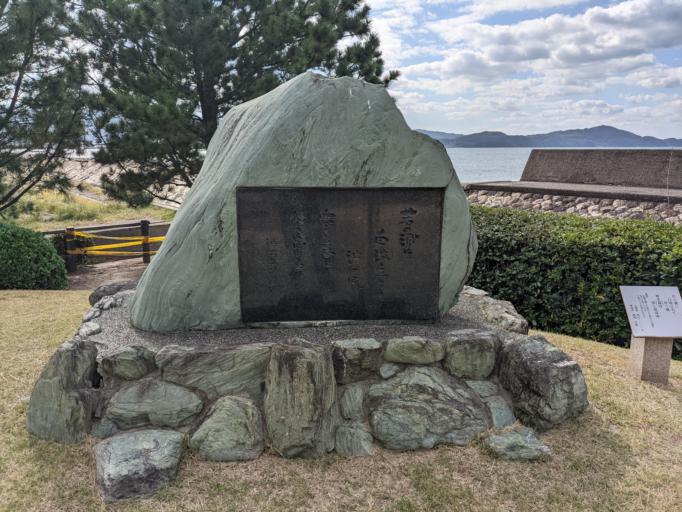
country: JP
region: Wakayama
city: Kainan
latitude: 34.1761
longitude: 135.1768
